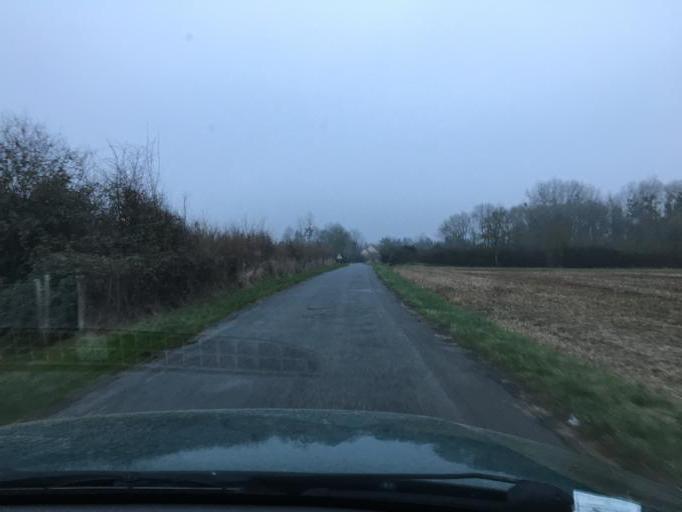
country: FR
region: Centre
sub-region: Departement du Loiret
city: Lailly-en-Val
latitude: 47.7610
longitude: 1.6687
